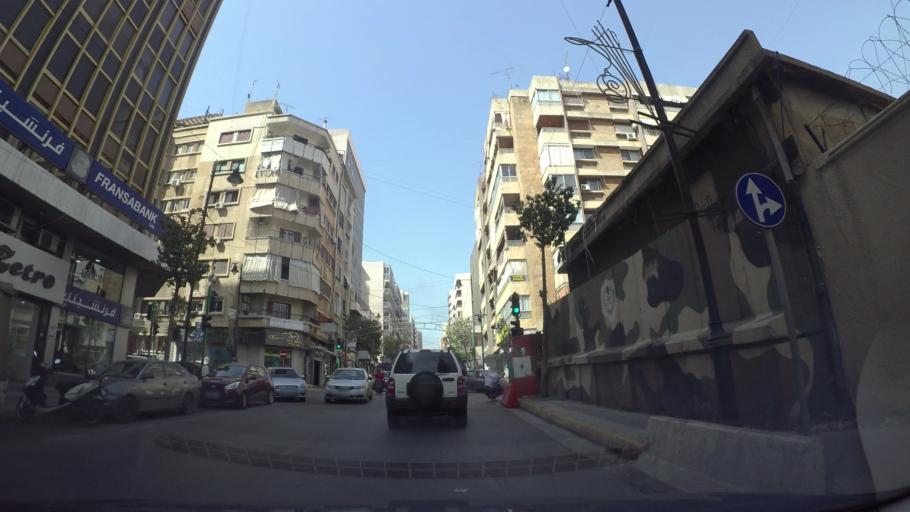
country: LB
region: Beyrouth
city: Beirut
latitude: 33.8818
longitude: 35.4909
